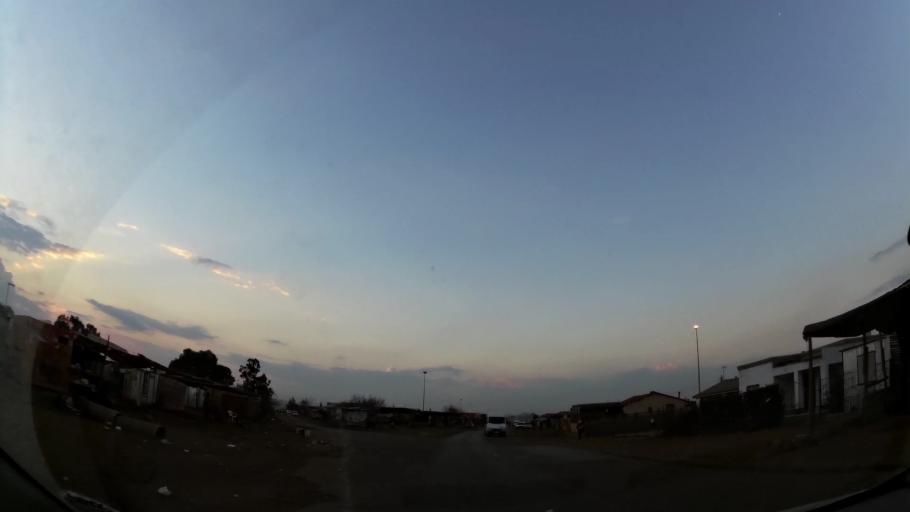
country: ZA
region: Gauteng
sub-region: City of Johannesburg Metropolitan Municipality
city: Orange Farm
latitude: -26.5582
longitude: 27.8617
